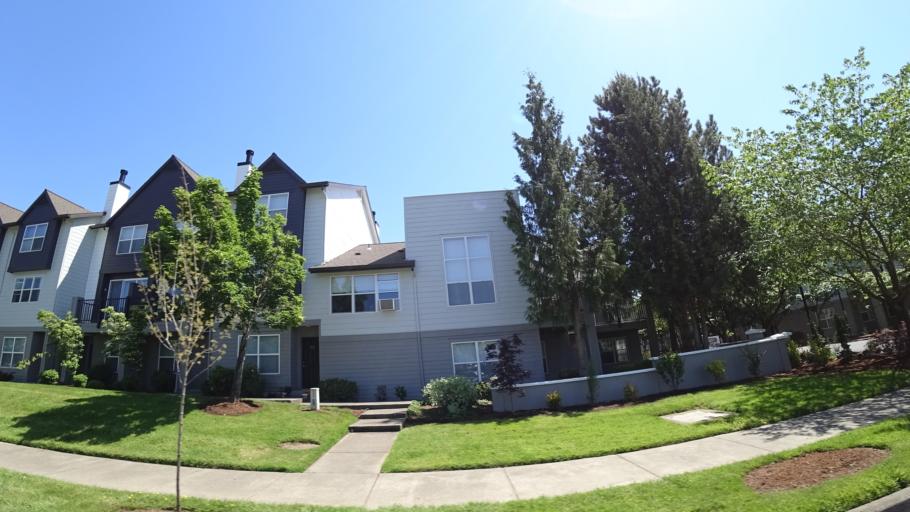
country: US
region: Oregon
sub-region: Washington County
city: Beaverton
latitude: 45.4978
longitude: -122.8336
